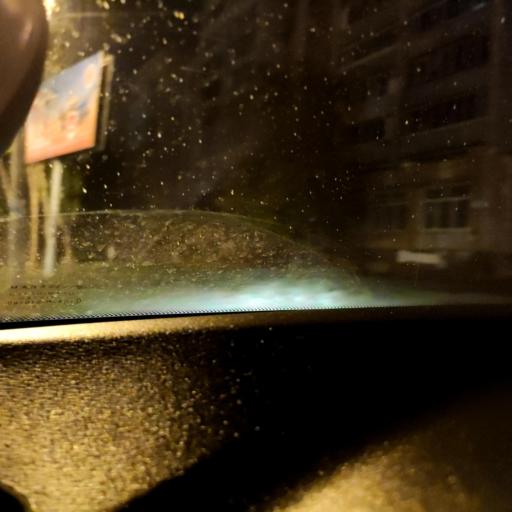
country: RU
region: Samara
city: Samara
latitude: 53.2170
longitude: 50.2217
